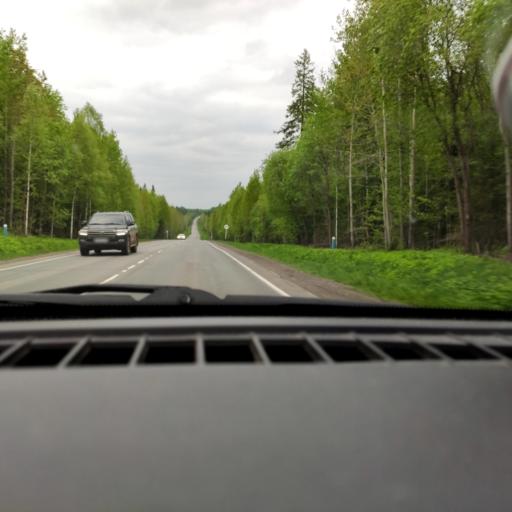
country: RU
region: Perm
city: Perm
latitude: 58.2264
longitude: 56.1637
